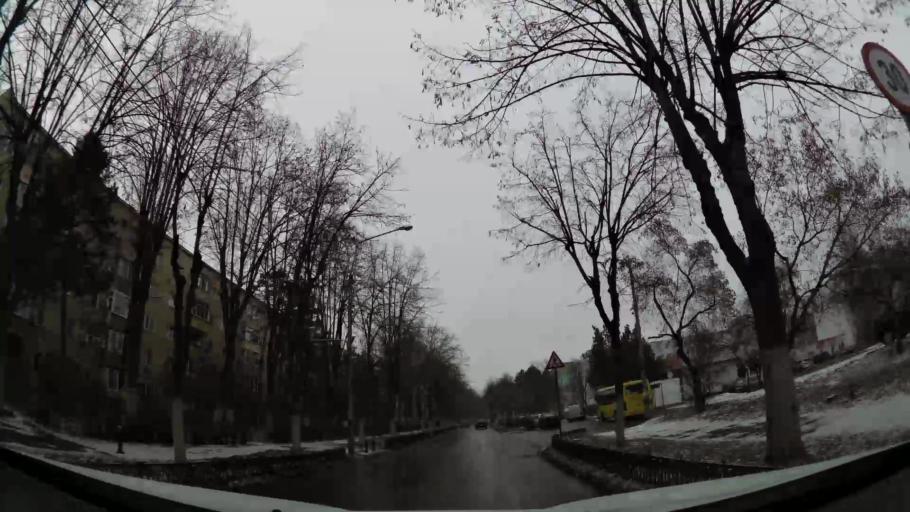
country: RO
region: Prahova
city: Ploiesti
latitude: 44.9566
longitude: 25.9975
